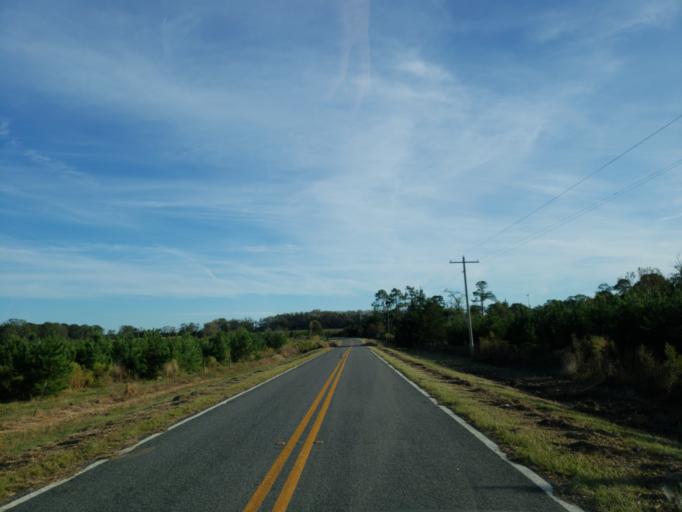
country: US
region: Georgia
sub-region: Dooly County
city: Vienna
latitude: 32.0354
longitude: -83.7524
